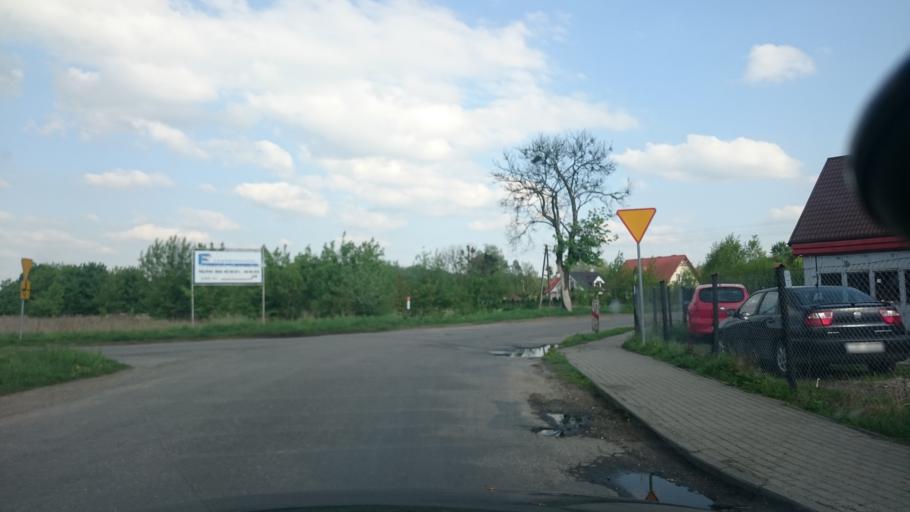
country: PL
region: Kujawsko-Pomorskie
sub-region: Grudziadz
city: Grudziadz
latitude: 53.4871
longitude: 18.8128
